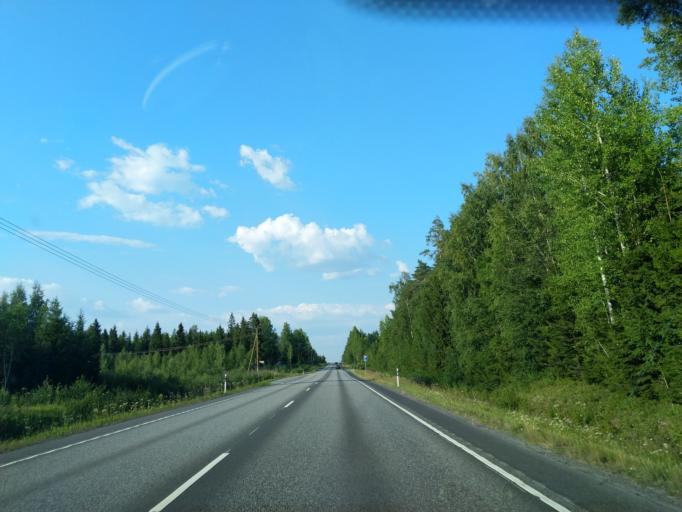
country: FI
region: Satakunta
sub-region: Pori
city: Pomarkku
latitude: 61.7175
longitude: 22.0479
